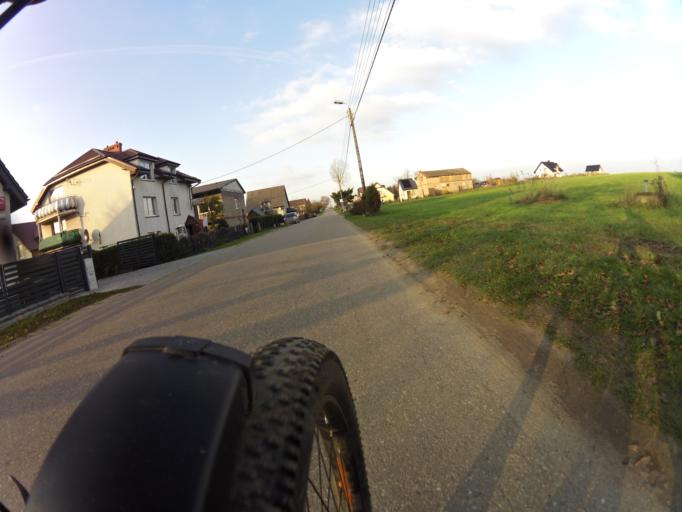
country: PL
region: Pomeranian Voivodeship
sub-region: Powiat pucki
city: Krokowa
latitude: 54.7635
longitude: 18.1816
